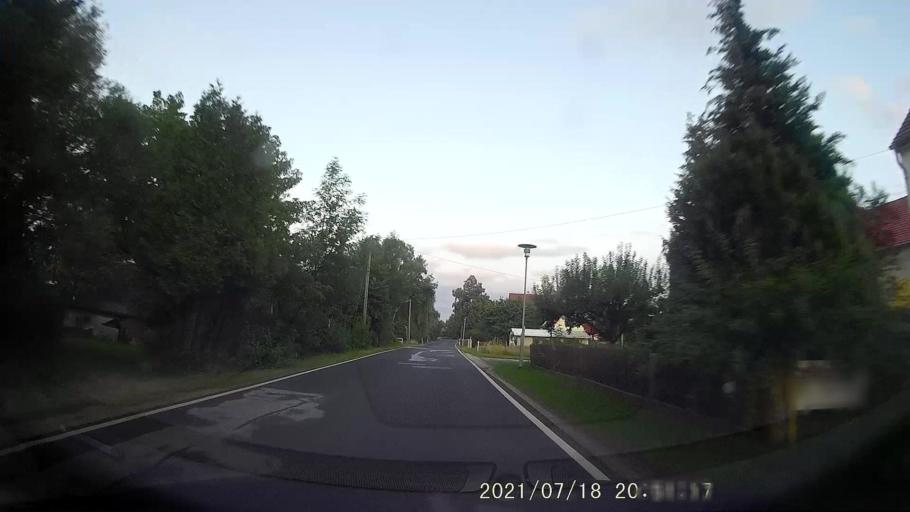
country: DE
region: Saxony
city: Konigshain
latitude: 51.1839
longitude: 14.8530
